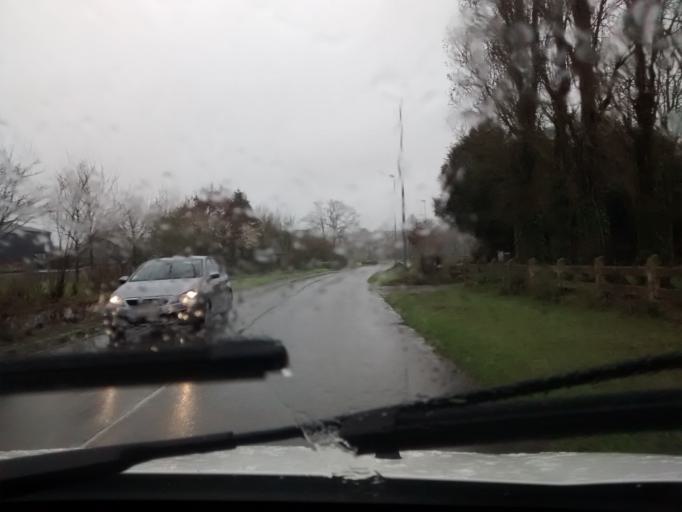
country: FR
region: Brittany
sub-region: Departement d'Ille-et-Vilaine
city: Acigne
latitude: 48.1270
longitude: -1.5327
